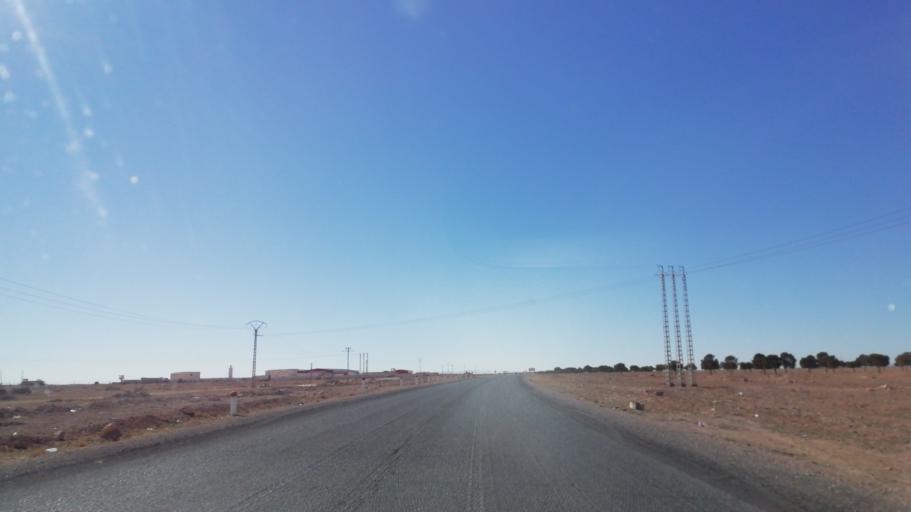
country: DZ
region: Saida
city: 'Ain el Hadjar
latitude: 34.0264
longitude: 0.0700
